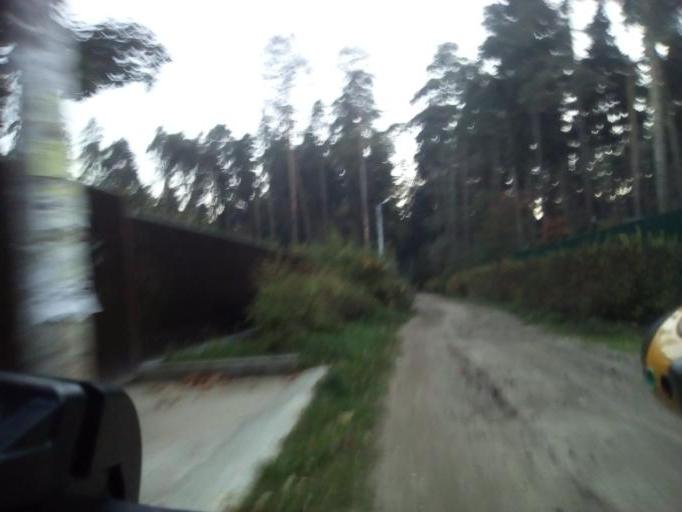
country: RU
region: Moskovskaya
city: Kratovo
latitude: 55.6092
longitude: 38.1613
